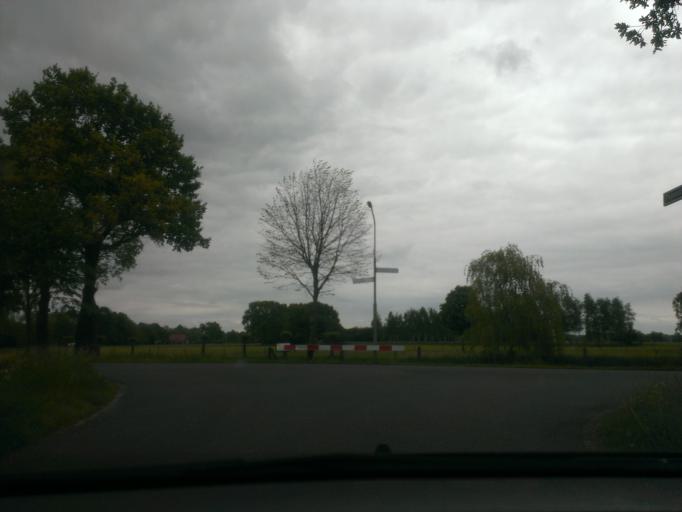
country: NL
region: Gelderland
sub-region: Gemeente Epe
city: Emst
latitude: 52.3351
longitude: 5.9667
